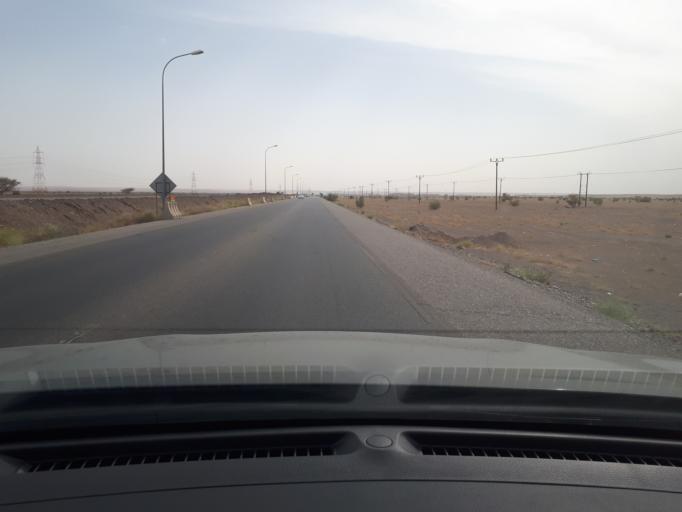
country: OM
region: Ash Sharqiyah
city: Badiyah
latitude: 22.4770
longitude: 58.9078
